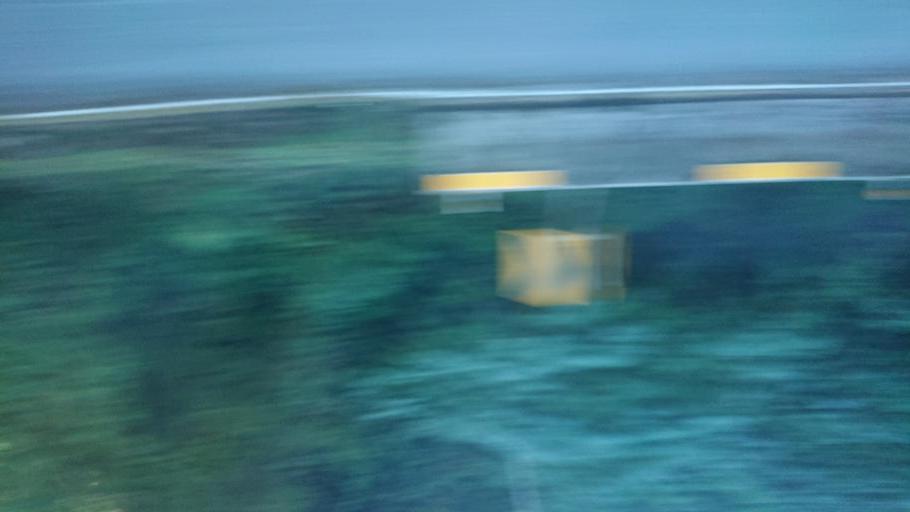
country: TW
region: Taiwan
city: Lugu
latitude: 23.4773
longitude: 120.8346
